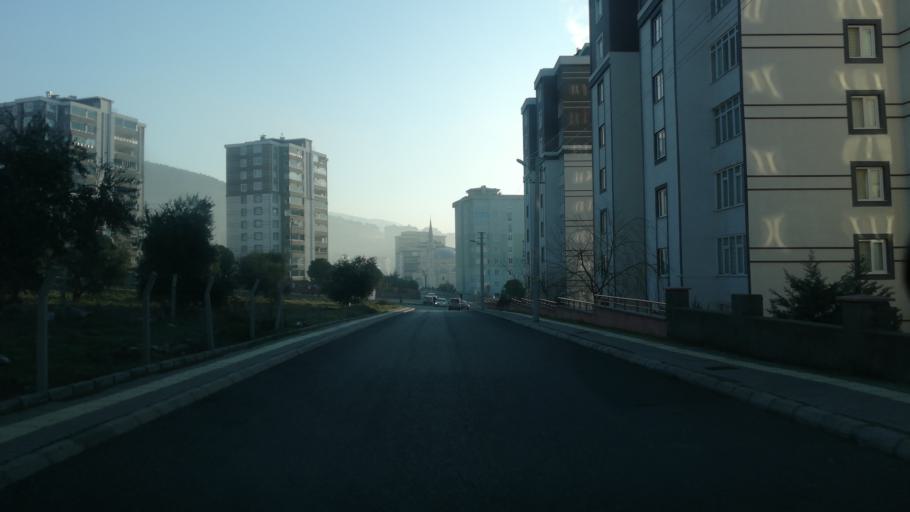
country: TR
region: Kahramanmaras
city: Kahramanmaras
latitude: 37.5974
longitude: 36.8957
